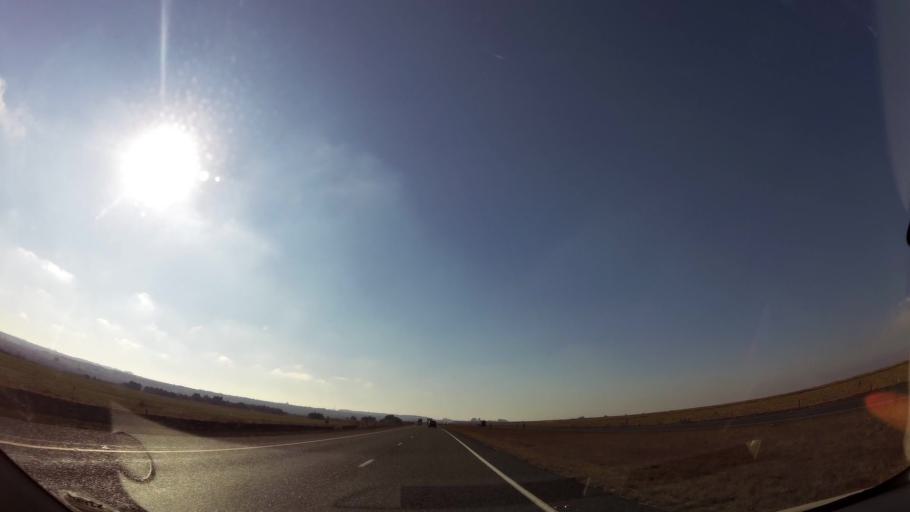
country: ZA
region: Mpumalanga
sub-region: Nkangala District Municipality
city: Delmas
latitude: -26.0192
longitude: 28.9264
